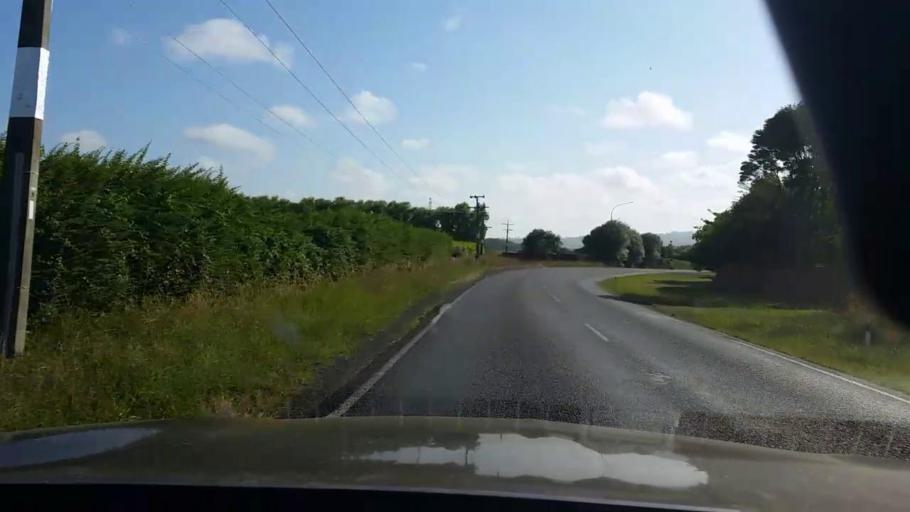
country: NZ
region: Waikato
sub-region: Hamilton City
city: Hamilton
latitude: -37.5900
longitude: 175.3876
